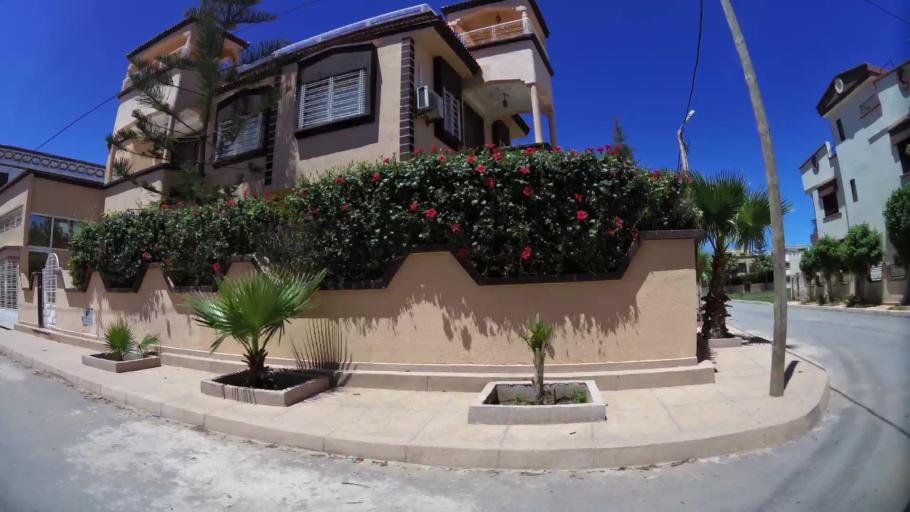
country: MA
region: Oriental
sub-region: Berkane-Taourirt
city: Madagh
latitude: 35.0857
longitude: -2.2434
